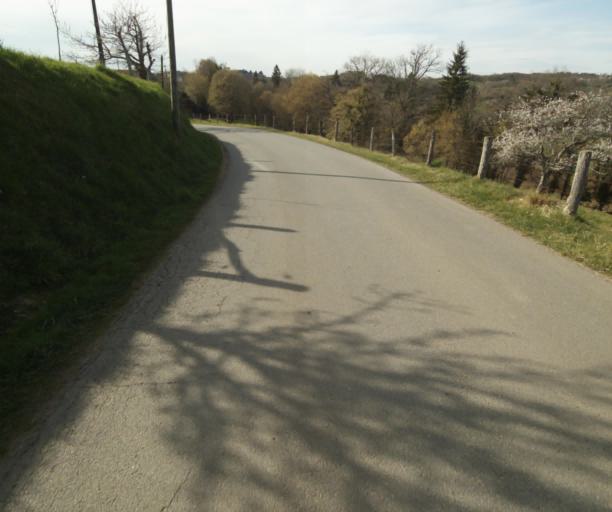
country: FR
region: Limousin
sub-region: Departement de la Correze
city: Naves
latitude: 45.3104
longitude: 1.7305
